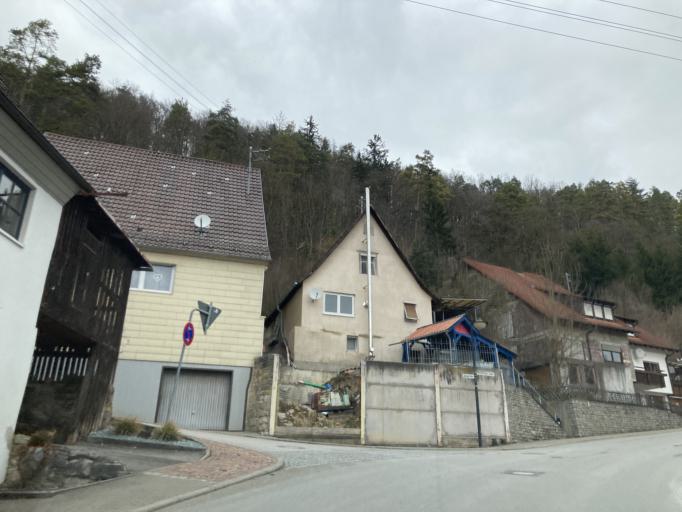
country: DE
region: Baden-Wuerttemberg
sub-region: Regierungsbezirk Stuttgart
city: Bondorf
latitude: 48.4491
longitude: 8.8024
